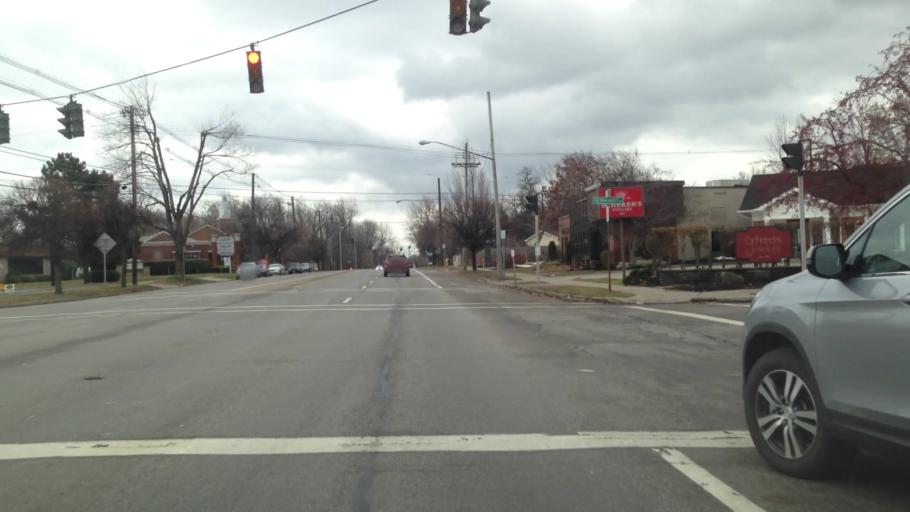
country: US
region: New York
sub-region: Erie County
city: Eggertsville
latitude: 42.9627
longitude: -78.7818
